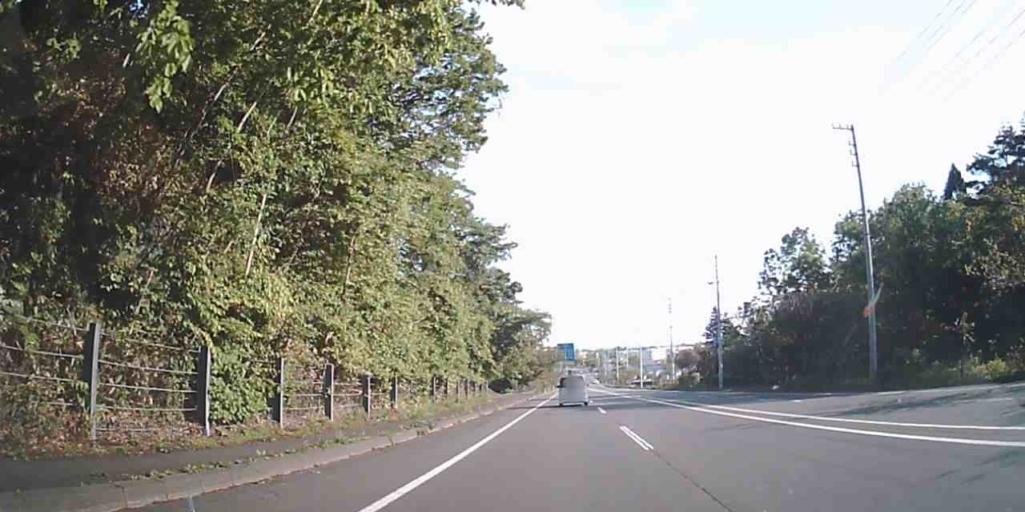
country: JP
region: Hokkaido
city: Shiraoi
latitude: 42.4602
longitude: 141.1778
